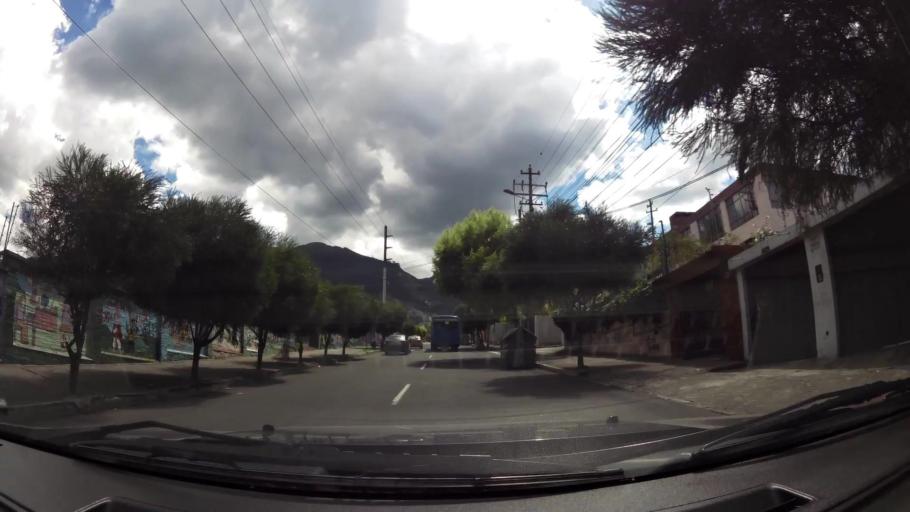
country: EC
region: Pichincha
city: Quito
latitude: -0.1899
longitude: -78.5031
